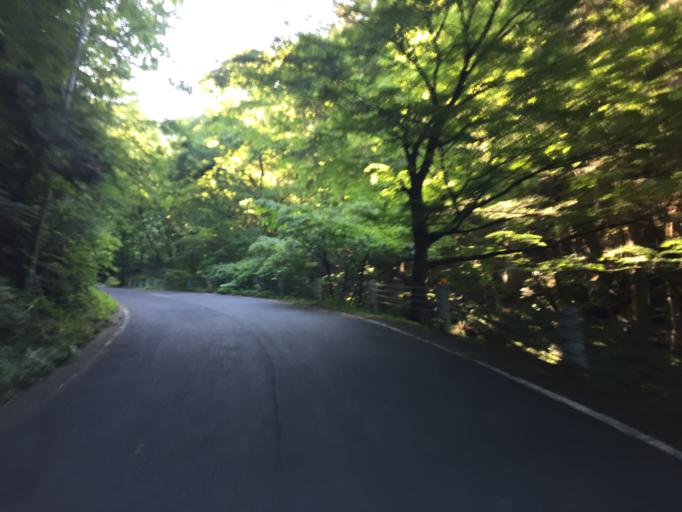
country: JP
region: Ibaraki
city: Kitaibaraki
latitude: 36.8816
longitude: 140.6317
